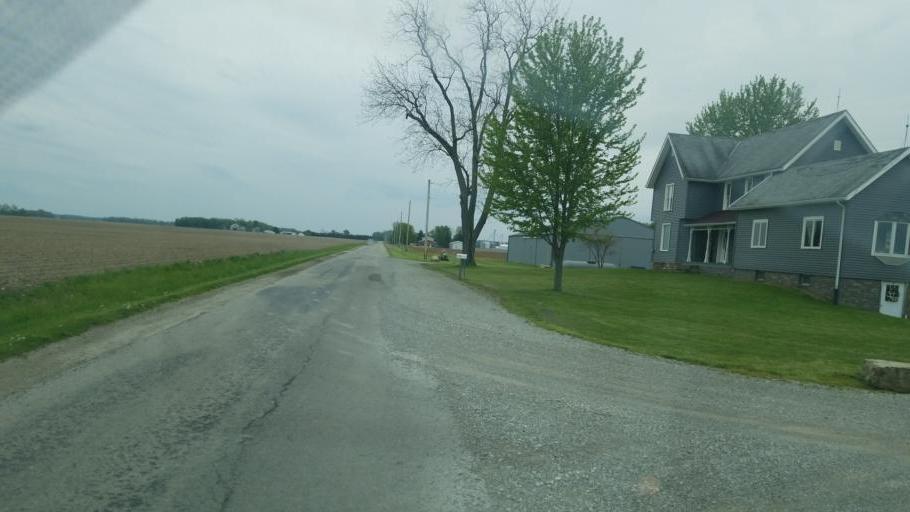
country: US
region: Ohio
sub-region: Huron County
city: Willard
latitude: 41.0212
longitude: -82.7989
